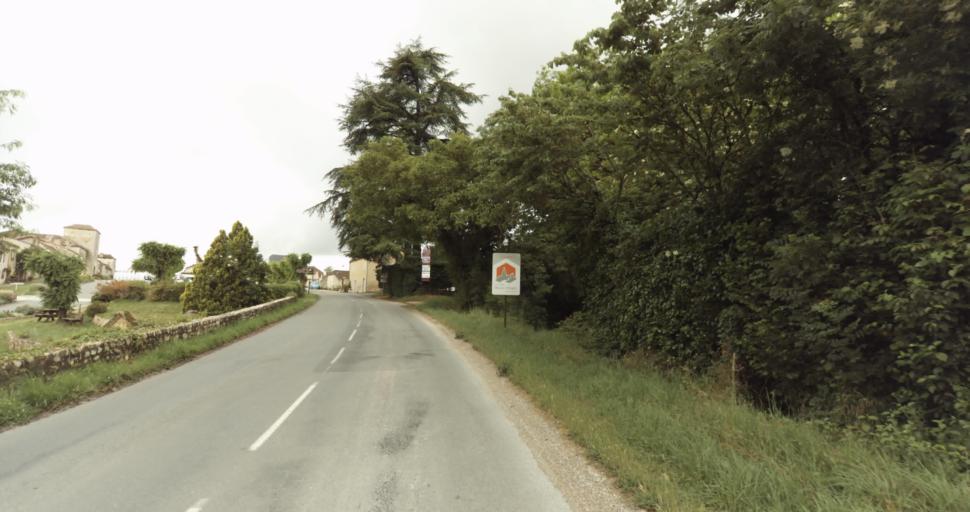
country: FR
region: Aquitaine
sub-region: Departement de la Dordogne
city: Belves
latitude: 44.6825
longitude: 0.8965
